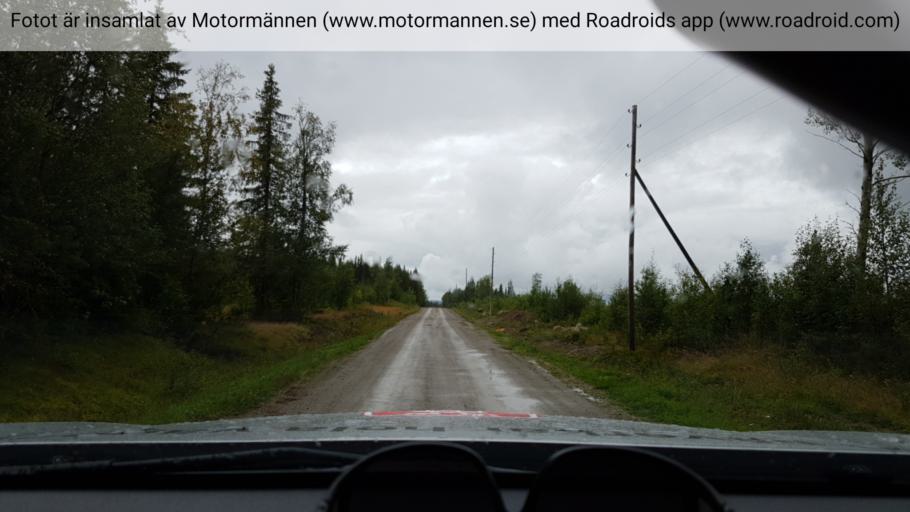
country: SE
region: Vaesterbotten
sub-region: Asele Kommun
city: Insjon
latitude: 64.7978
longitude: 17.4949
